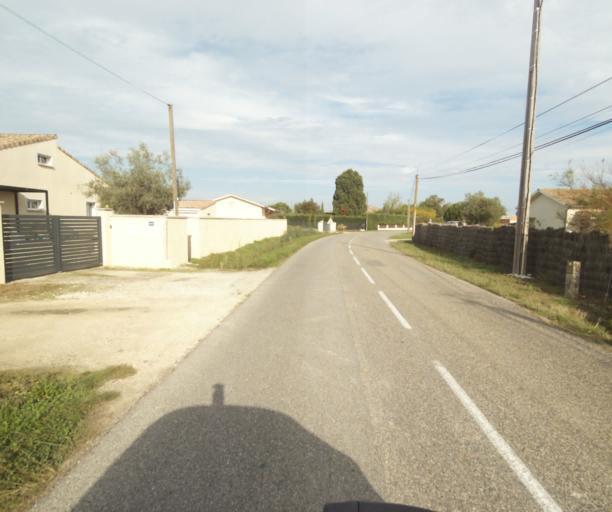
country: FR
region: Midi-Pyrenees
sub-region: Departement du Tarn-et-Garonne
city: Montech
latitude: 43.9685
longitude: 1.2320
